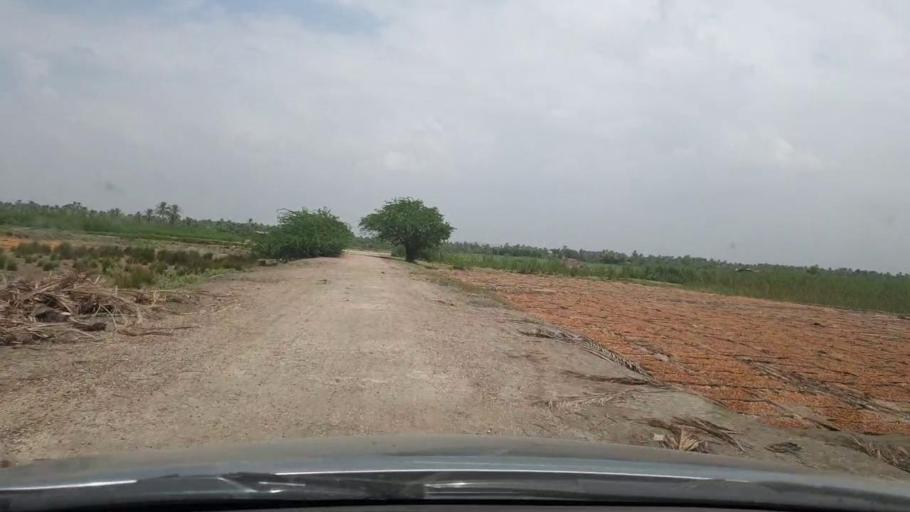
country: PK
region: Sindh
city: Kot Diji
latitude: 27.4271
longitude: 68.7605
